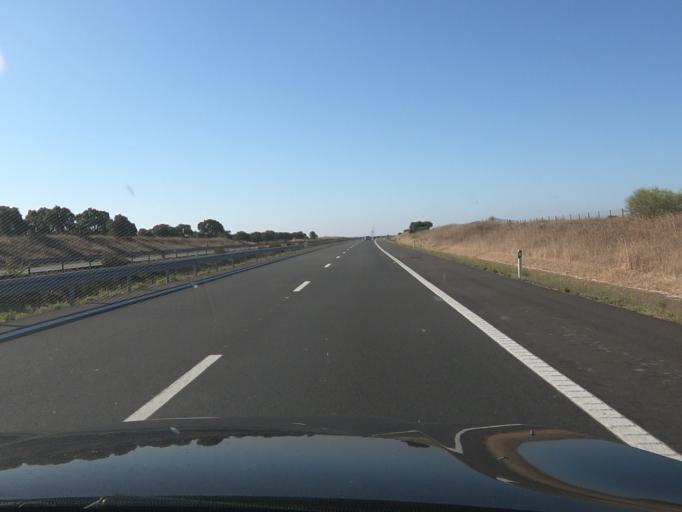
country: PT
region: Beja
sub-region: Aljustrel
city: Aljustrel
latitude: 38.0196
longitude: -8.2829
